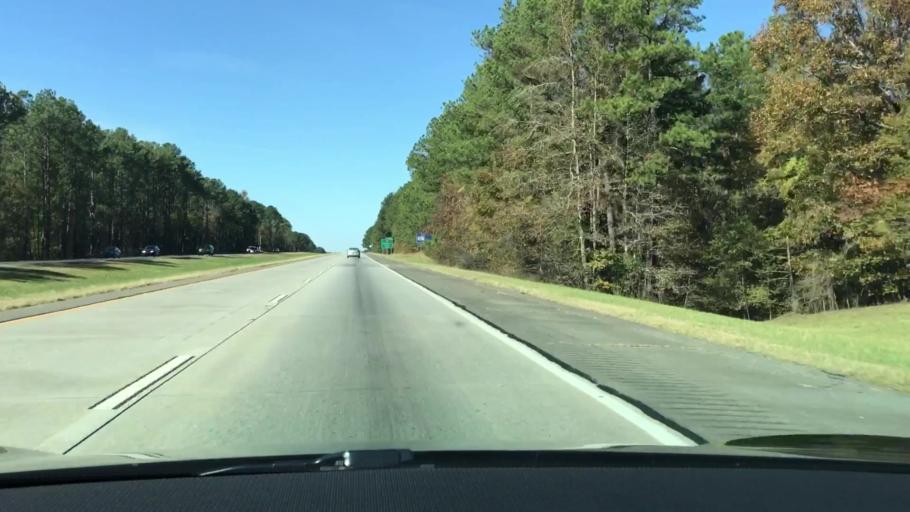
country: US
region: Georgia
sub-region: Taliaferro County
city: Crawfordville
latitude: 33.5260
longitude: -82.8847
